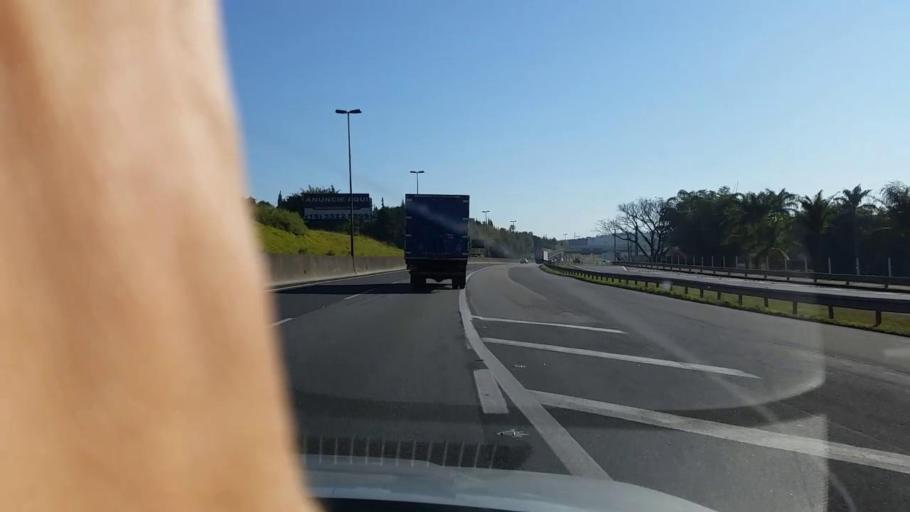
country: BR
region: Sao Paulo
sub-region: Varzea Paulista
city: Varzea Paulista
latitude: -23.2574
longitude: -46.8673
